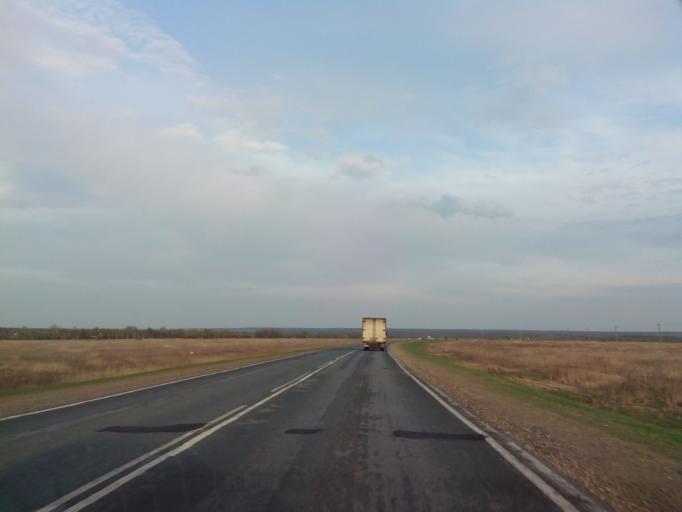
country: RU
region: Rjazan
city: Korablino
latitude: 53.7446
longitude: 39.8796
